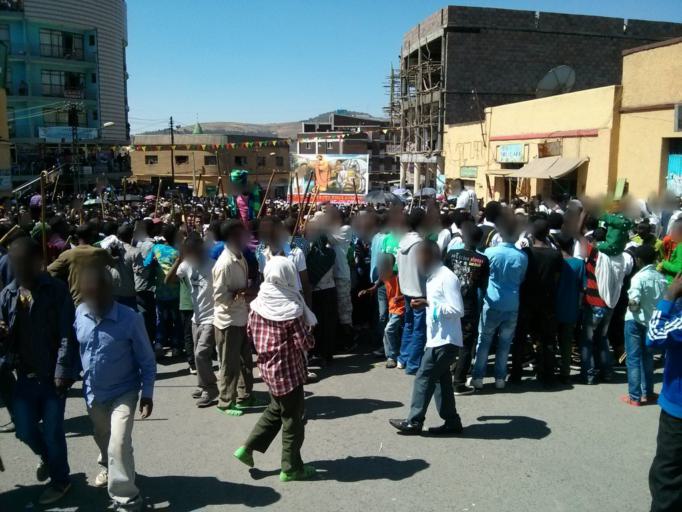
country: ET
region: Amhara
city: Gondar
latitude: 12.6120
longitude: 37.4695
